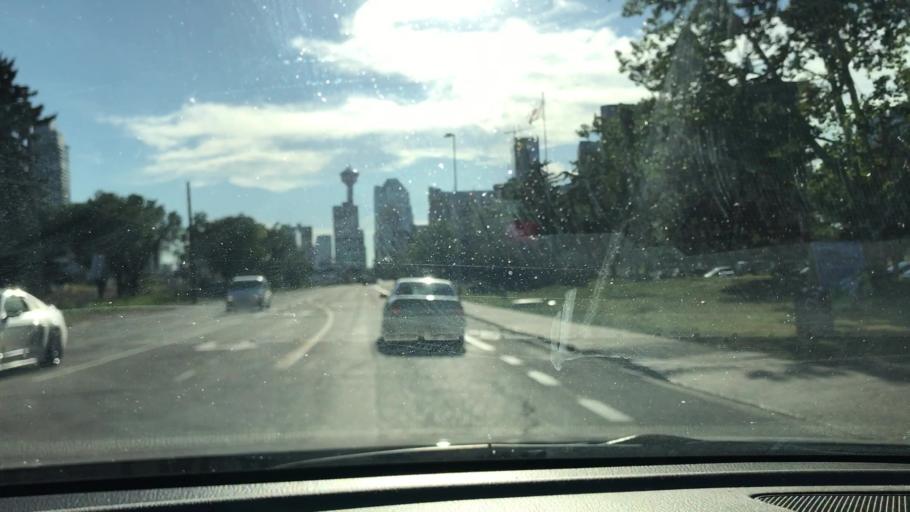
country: CA
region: Alberta
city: Calgary
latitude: 51.0439
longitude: -114.0441
